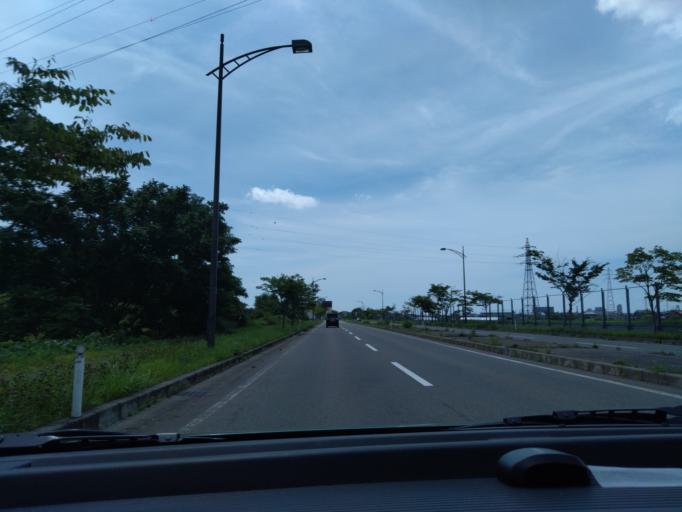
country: JP
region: Akita
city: Akita
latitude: 39.7200
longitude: 140.1598
